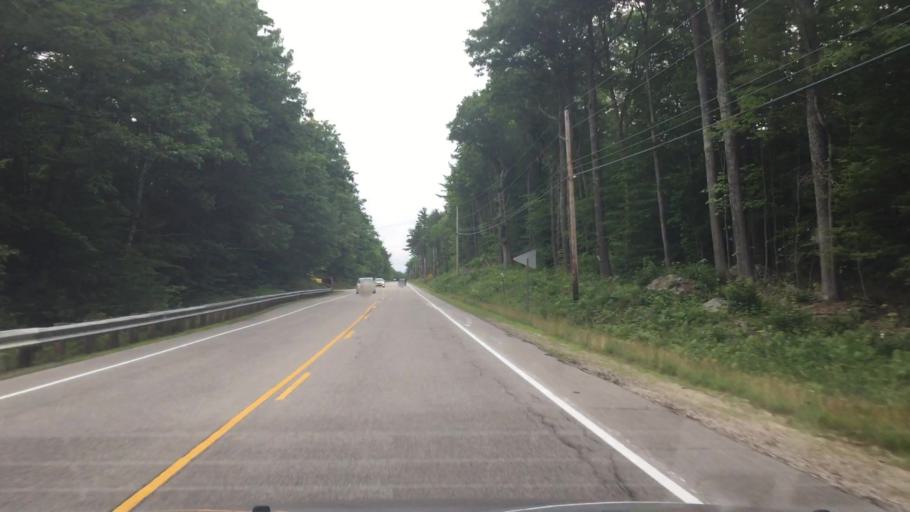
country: US
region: New Hampshire
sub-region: Carroll County
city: Sandwich
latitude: 43.7876
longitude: -71.3773
